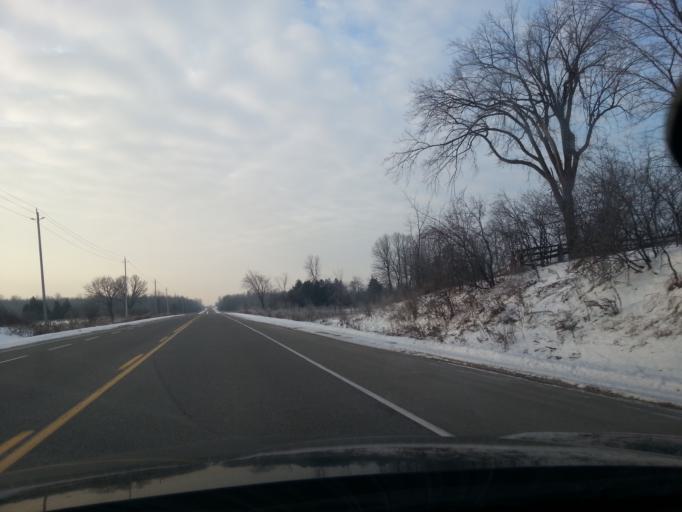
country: CA
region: Ontario
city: Perth
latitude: 44.9535
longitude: -76.2348
